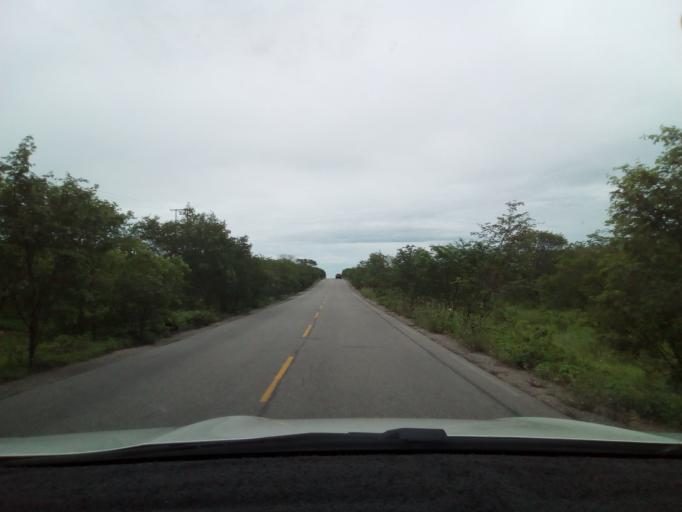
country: BR
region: Rio Grande do Norte
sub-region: Caraubas
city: Caraubas
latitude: -5.8396
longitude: -37.6243
